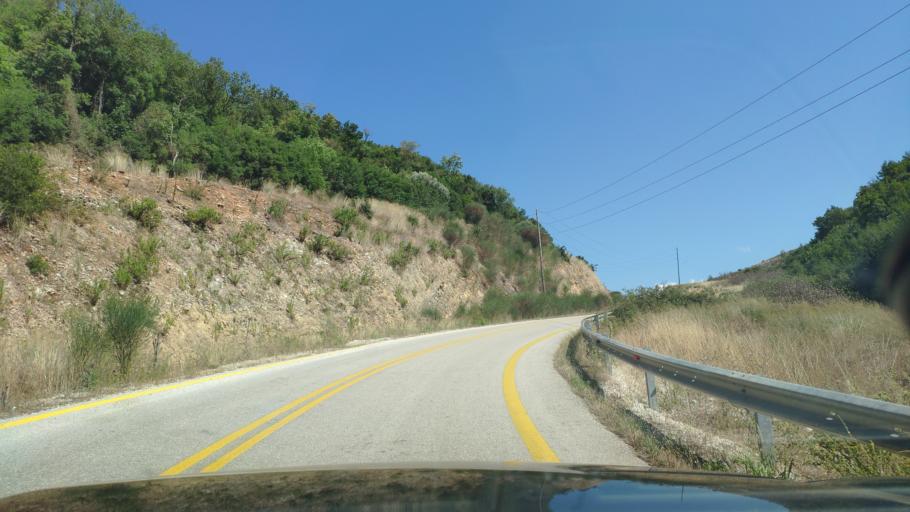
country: GR
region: West Greece
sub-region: Nomos Aitolias kai Akarnanias
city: Amfilochia
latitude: 38.8592
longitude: 21.0848
